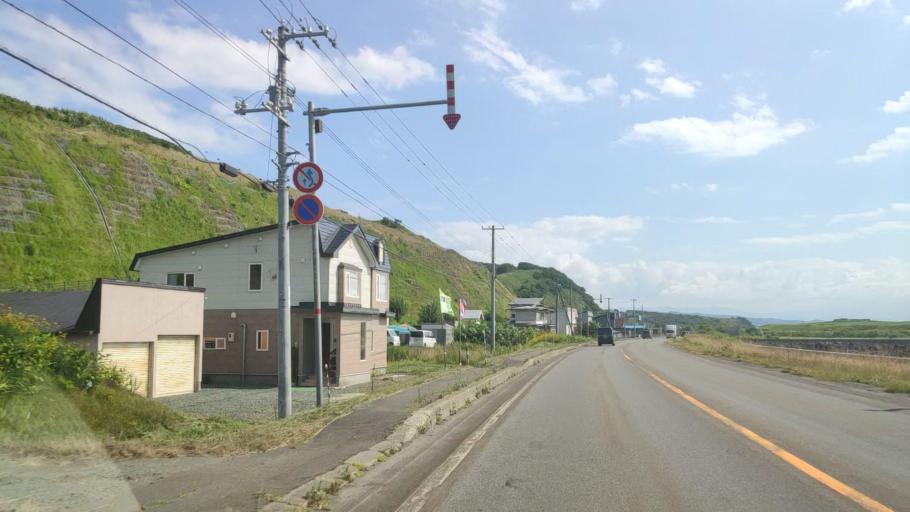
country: JP
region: Hokkaido
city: Rumoi
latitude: 43.9777
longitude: 141.6466
